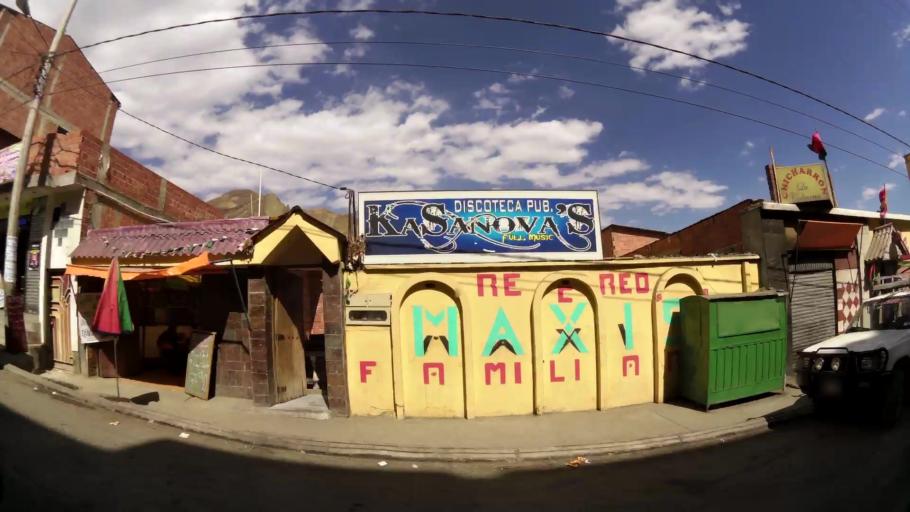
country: BO
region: La Paz
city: La Paz
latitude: -16.4610
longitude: -68.1046
